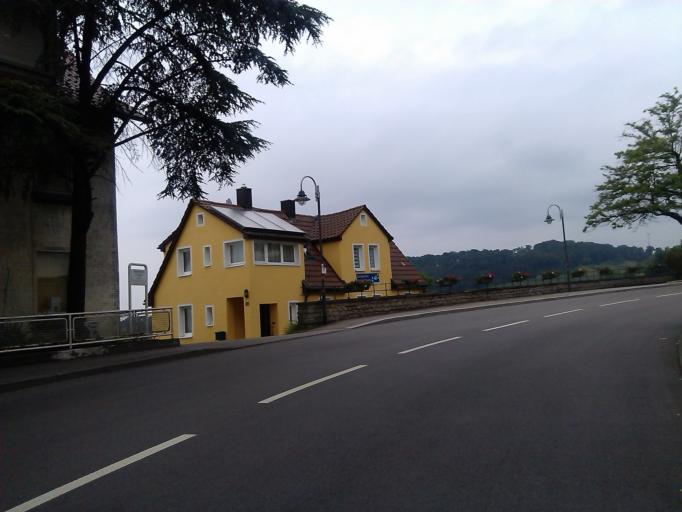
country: DE
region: Baden-Wuerttemberg
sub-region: Regierungsbezirk Stuttgart
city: Lowenstein
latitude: 49.0959
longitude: 9.3801
